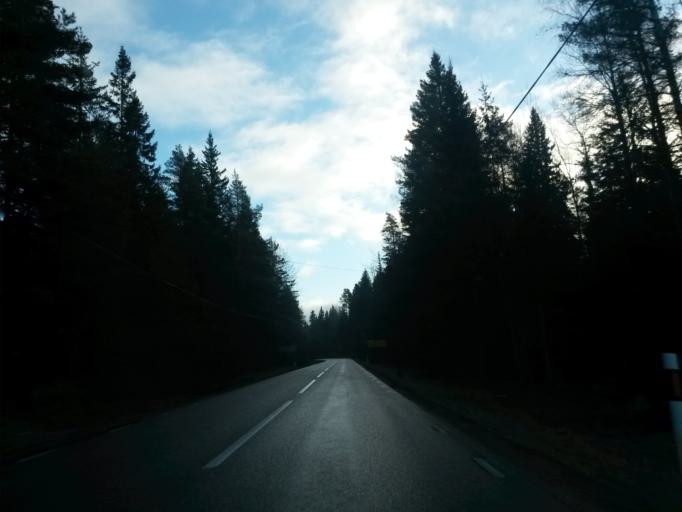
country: SE
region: Vaestra Goetaland
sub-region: Boras Kommun
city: Boras
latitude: 57.8505
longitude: 12.9481
